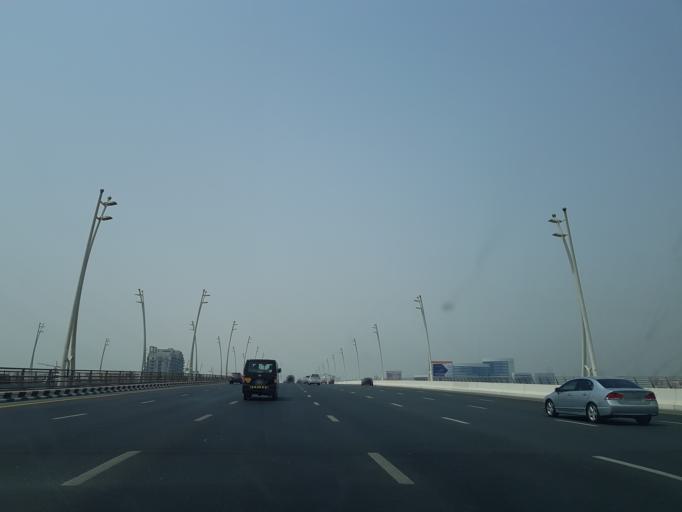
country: AE
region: Ash Shariqah
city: Sharjah
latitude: 25.2350
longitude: 55.3388
